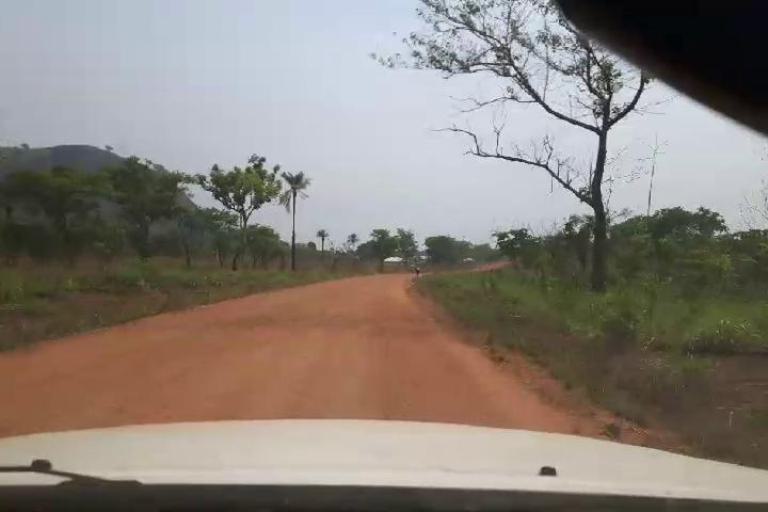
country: SL
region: Northern Province
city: Bumbuna
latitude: 8.9514
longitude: -11.8064
